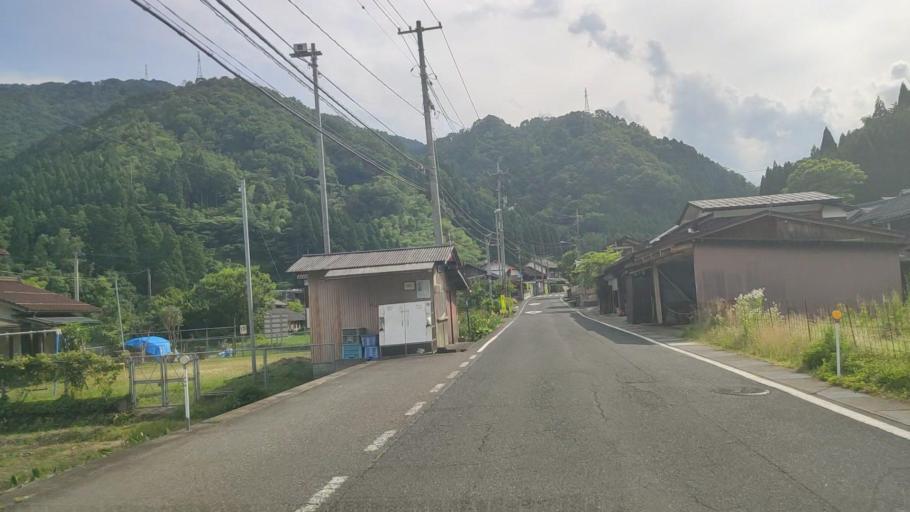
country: JP
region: Tottori
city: Tottori
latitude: 35.3353
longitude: 134.1428
